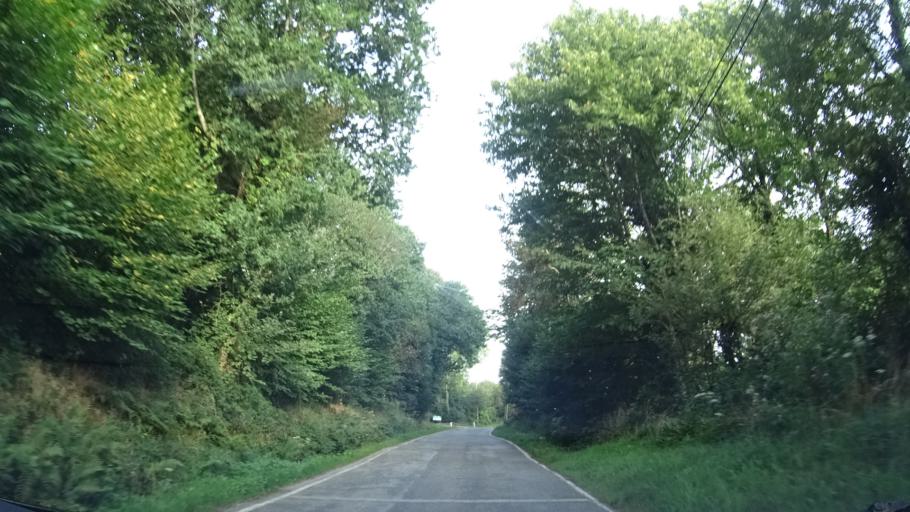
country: FR
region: Brittany
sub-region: Departement du Finistere
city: Chateaulin
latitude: 48.1972
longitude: -4.1056
